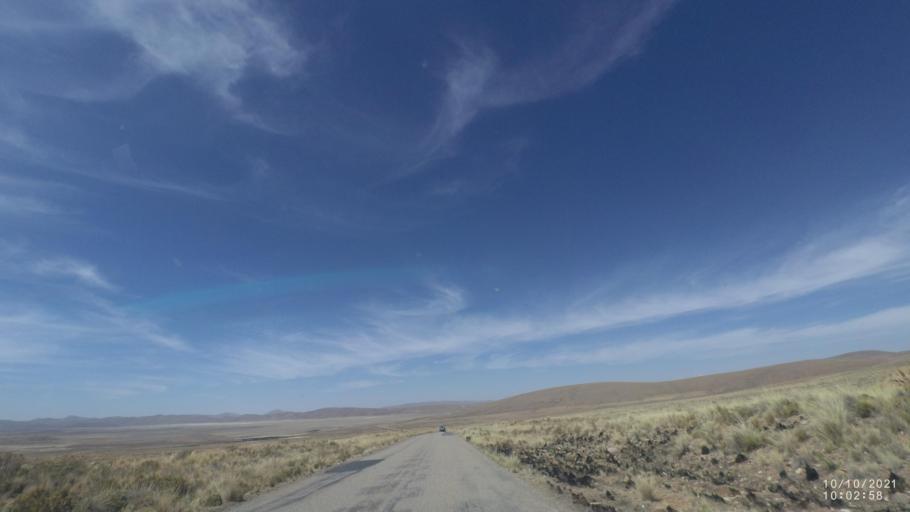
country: BO
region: La Paz
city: Eucaliptus
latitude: -17.3632
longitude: -67.4373
